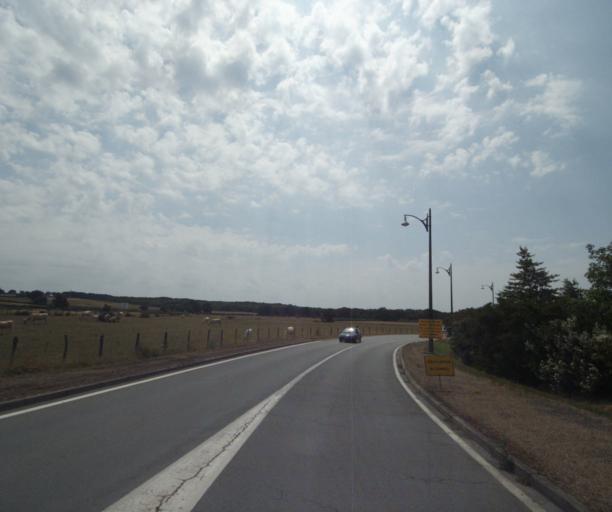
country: FR
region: Bourgogne
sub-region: Departement de Saone-et-Loire
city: Gueugnon
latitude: 46.5845
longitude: 4.0634
